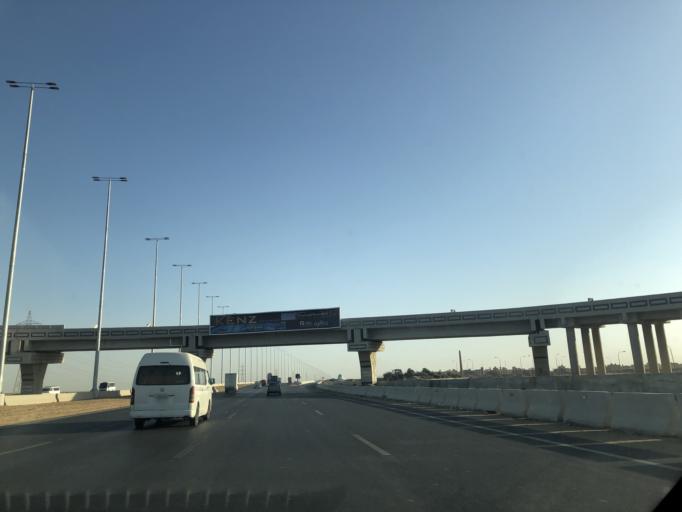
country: EG
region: Al Jizah
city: Madinat Sittah Uktubar
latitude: 29.9273
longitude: 31.0961
